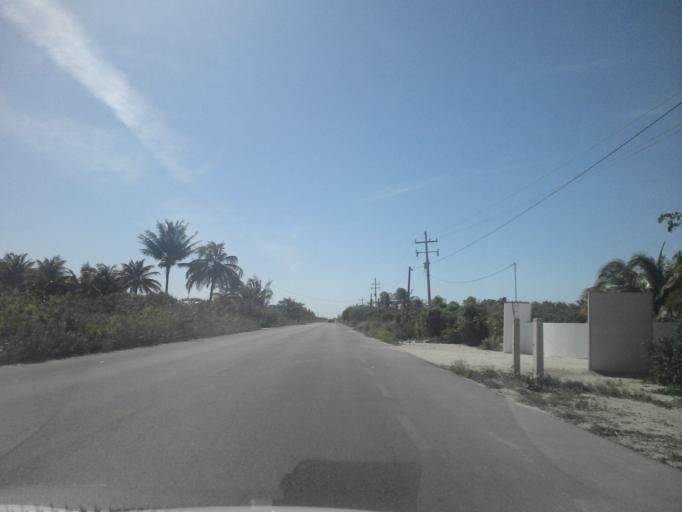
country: MX
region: Yucatan
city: Telchac Puerto
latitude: 21.3270
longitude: -89.4069
